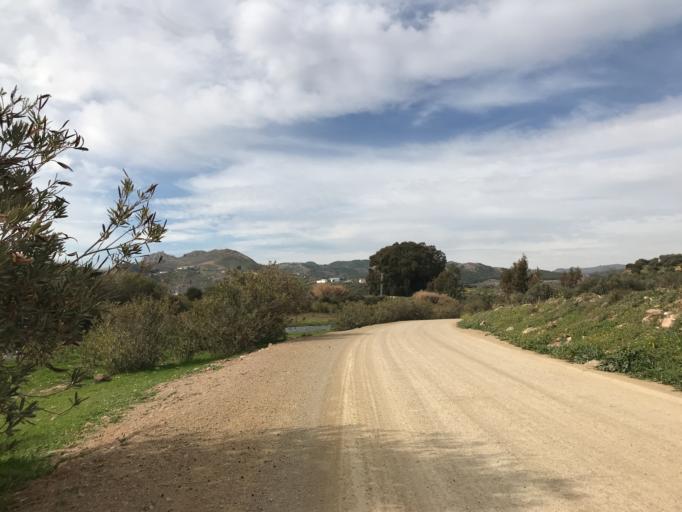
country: ES
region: Andalusia
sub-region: Provincia de Malaga
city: Ardales
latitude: 36.8827
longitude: -4.8528
